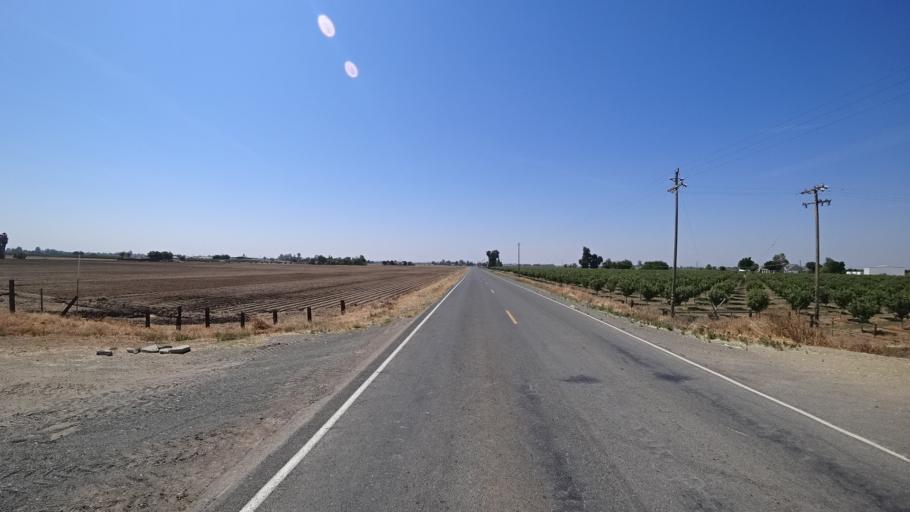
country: US
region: California
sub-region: Fresno County
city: Riverdale
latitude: 36.3852
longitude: -119.8515
